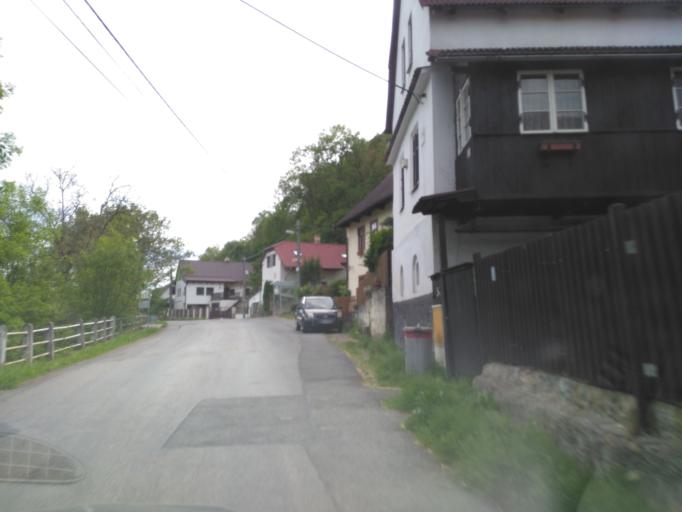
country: CZ
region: Central Bohemia
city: Zdice
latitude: 49.8946
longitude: 13.9599
